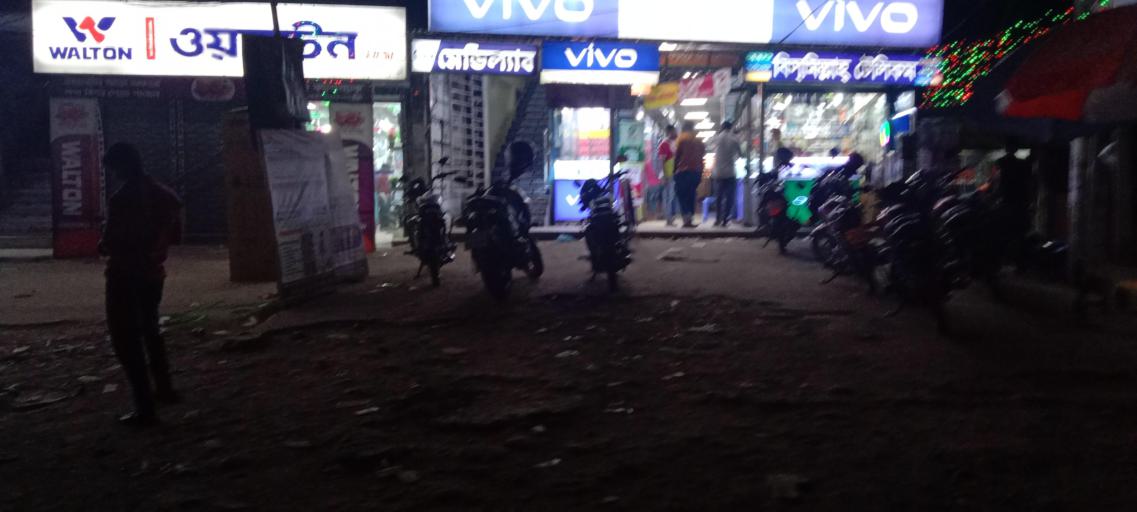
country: BD
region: Dhaka
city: Gafargaon
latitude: 24.4060
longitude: 90.3860
